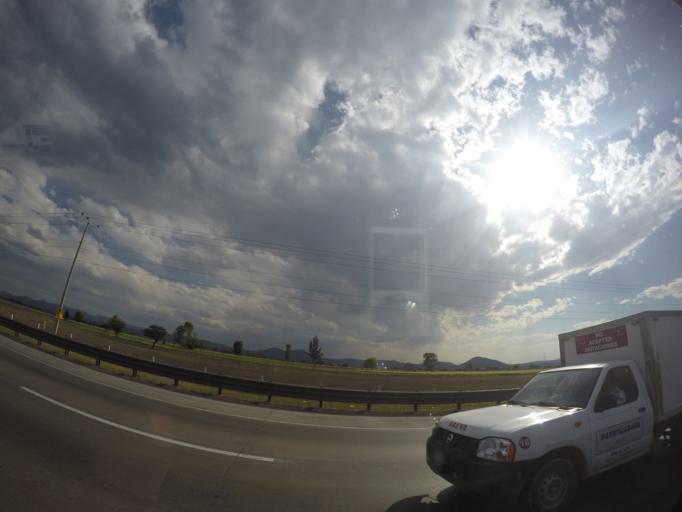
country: MX
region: Queretaro
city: El Sauz
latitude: 20.4704
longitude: -100.1058
